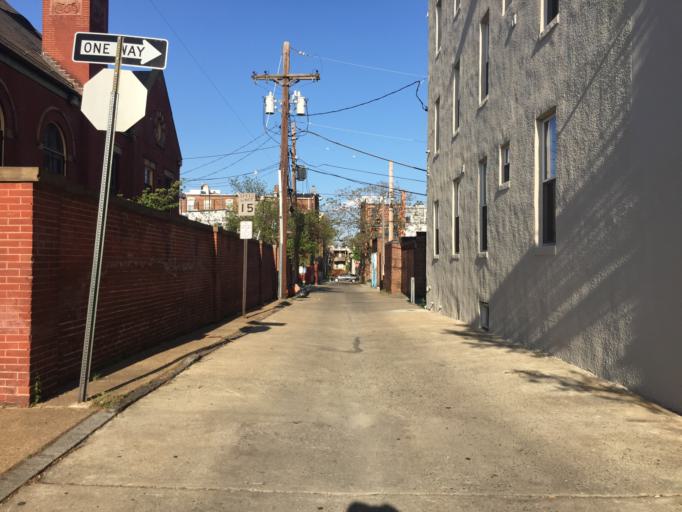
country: US
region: Maryland
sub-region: City of Baltimore
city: Baltimore
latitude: 39.3185
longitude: -76.6154
